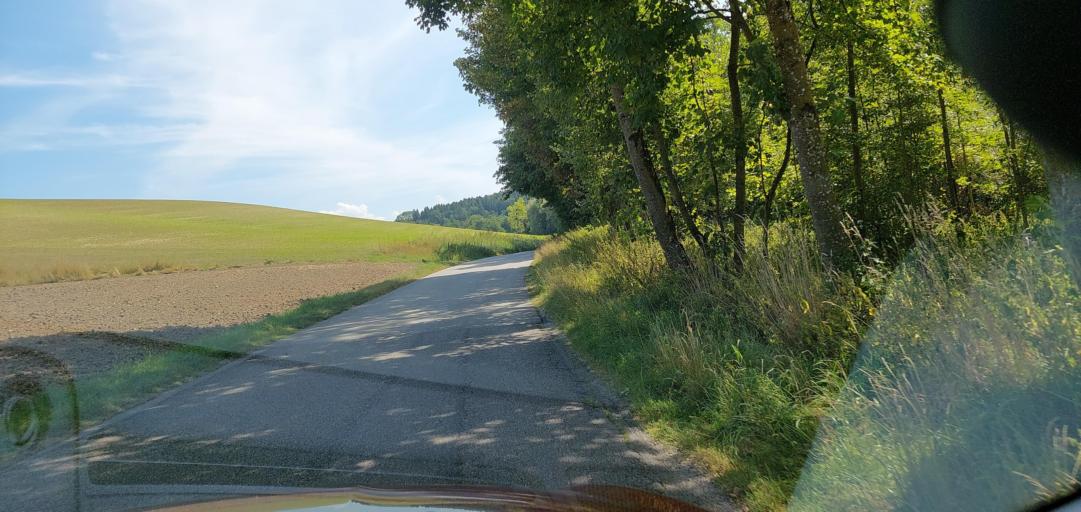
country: AT
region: Upper Austria
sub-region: Wels-Land
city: Edt bei Lambach
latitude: 48.1317
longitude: 13.8886
